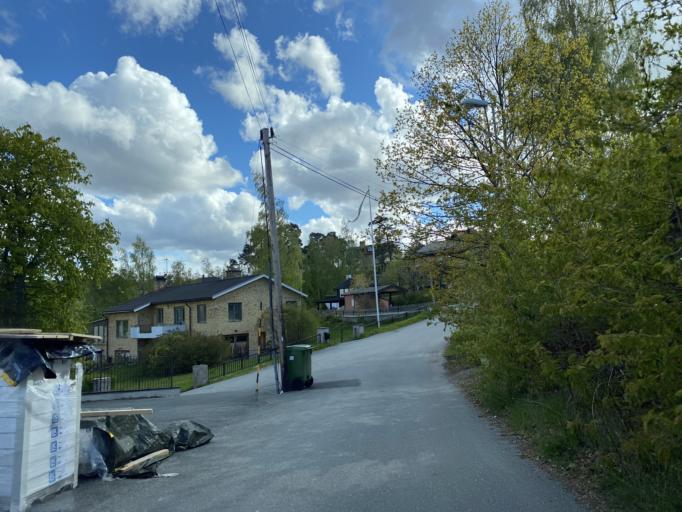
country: SE
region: Stockholm
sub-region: Sollentuna Kommun
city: Sollentuna
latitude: 59.4256
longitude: 17.9730
